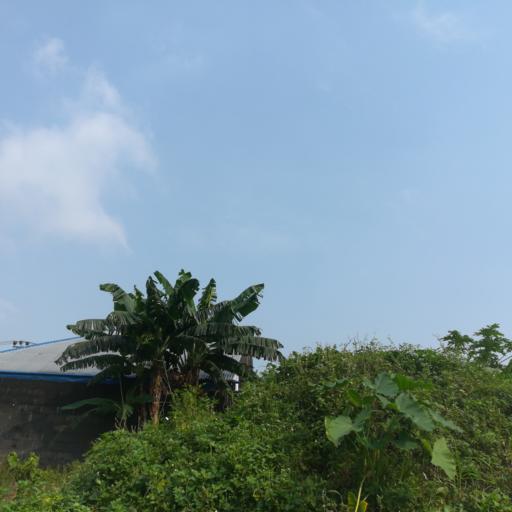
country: NG
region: Rivers
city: Port Harcourt
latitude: 4.8411
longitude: 7.0635
